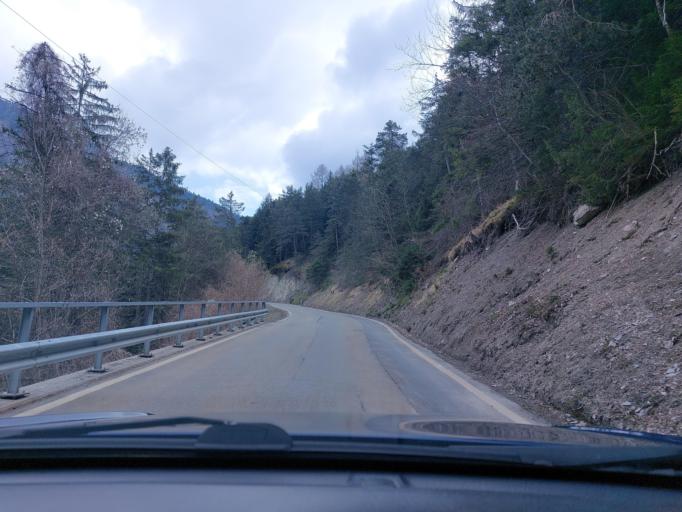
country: CH
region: Valais
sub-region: Sion District
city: Saviese
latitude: 46.2680
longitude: 7.3131
